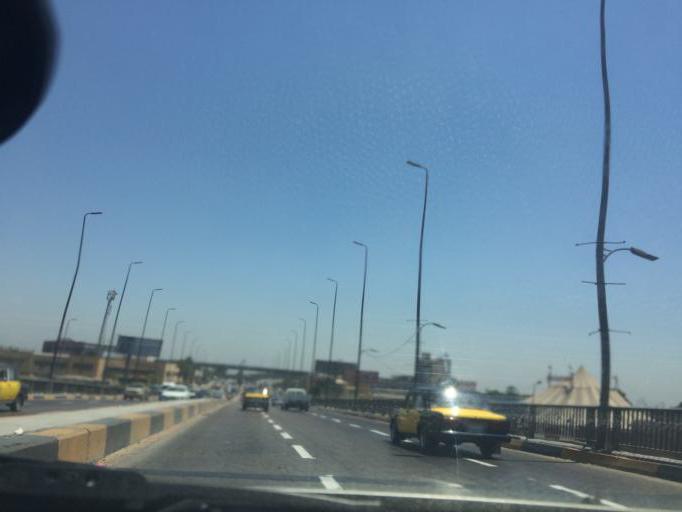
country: EG
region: Alexandria
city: Alexandria
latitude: 31.1858
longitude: 29.9255
